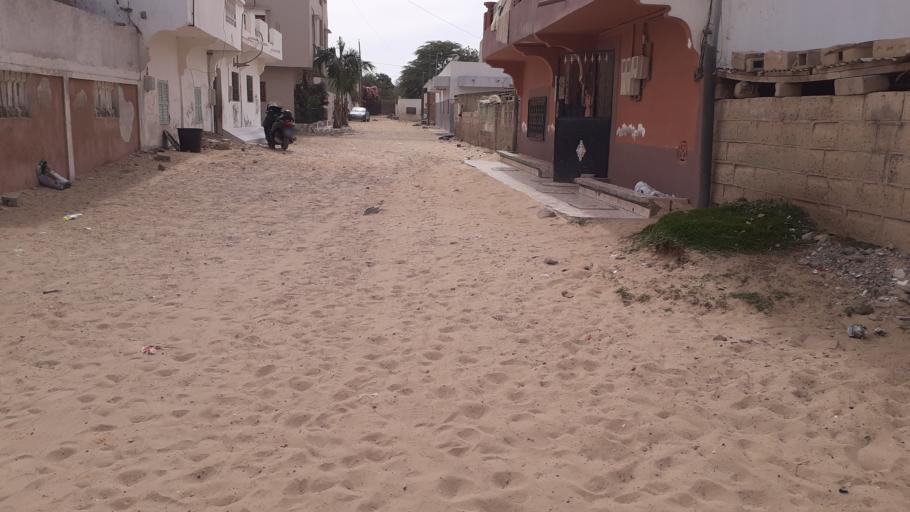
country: SN
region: Saint-Louis
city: Saint-Louis
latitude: 16.0242
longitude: -16.4859
